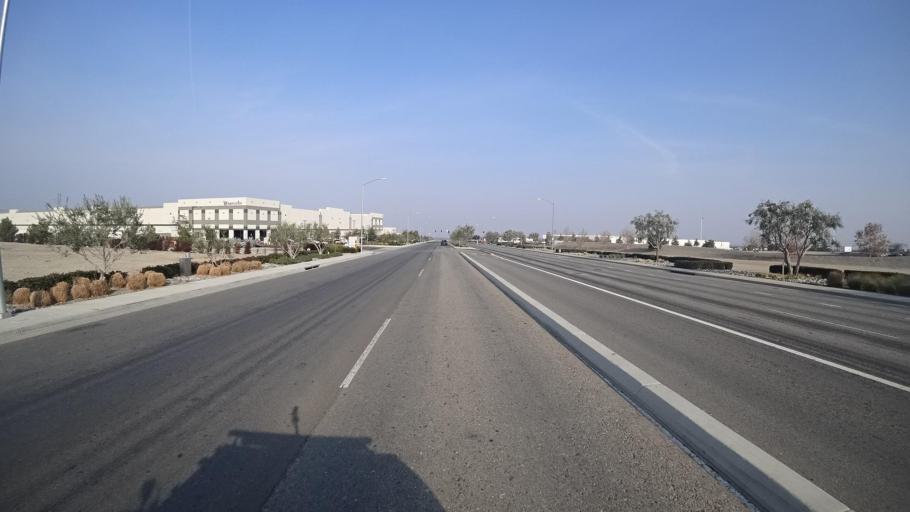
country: US
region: California
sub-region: Kern County
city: Lebec
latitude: 34.9934
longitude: -118.9426
